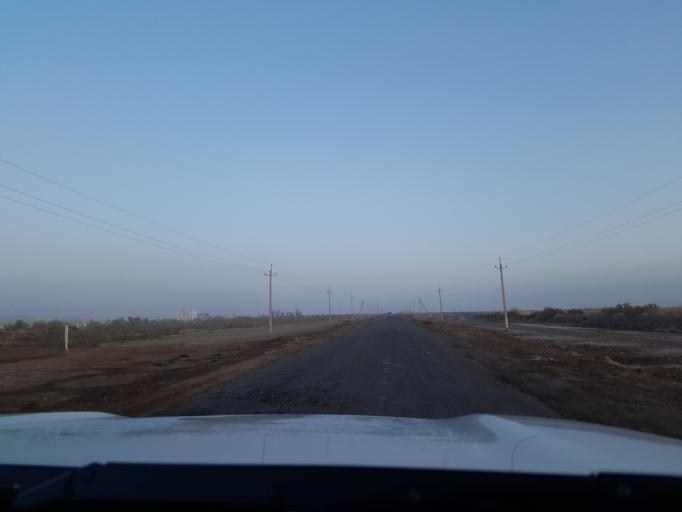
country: TM
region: Dasoguz
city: Koeneuergench
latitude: 41.8164
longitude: 58.7035
